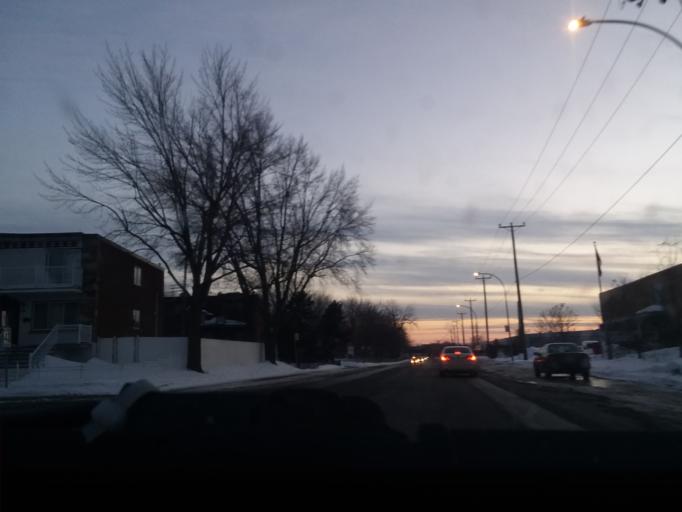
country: CA
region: Quebec
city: Montreal-Ouest
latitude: 45.4393
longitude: -73.6331
